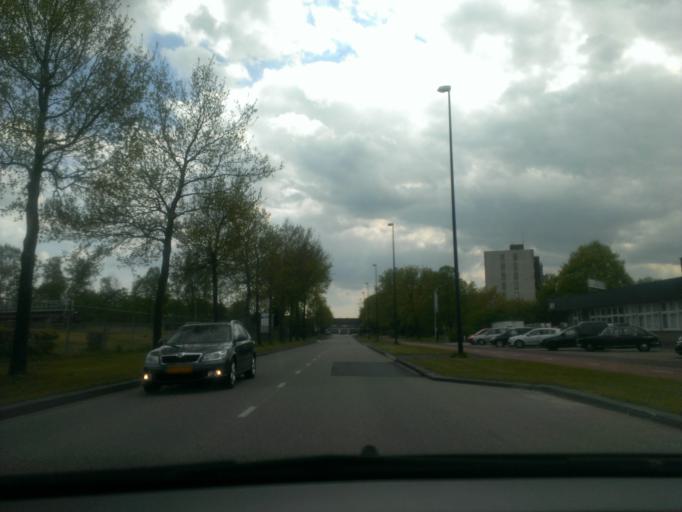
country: NL
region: Gelderland
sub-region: Gemeente Apeldoorn
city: Apeldoorn
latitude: 52.2377
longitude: 5.9698
